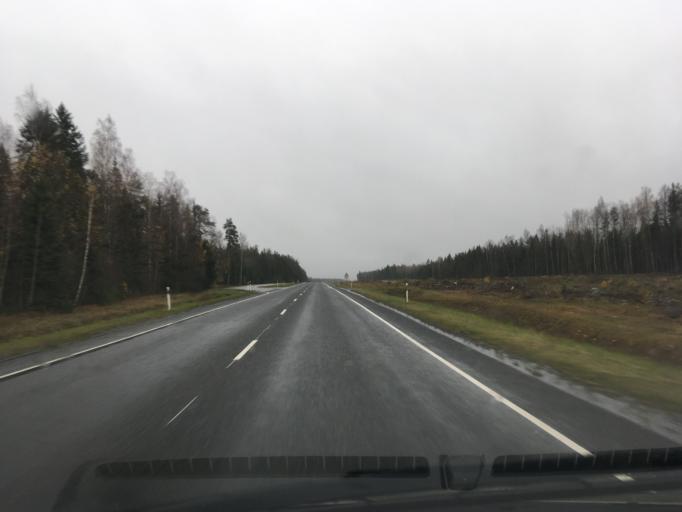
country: EE
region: Harju
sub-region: Nissi vald
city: Turba
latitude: 58.9619
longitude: 24.0727
